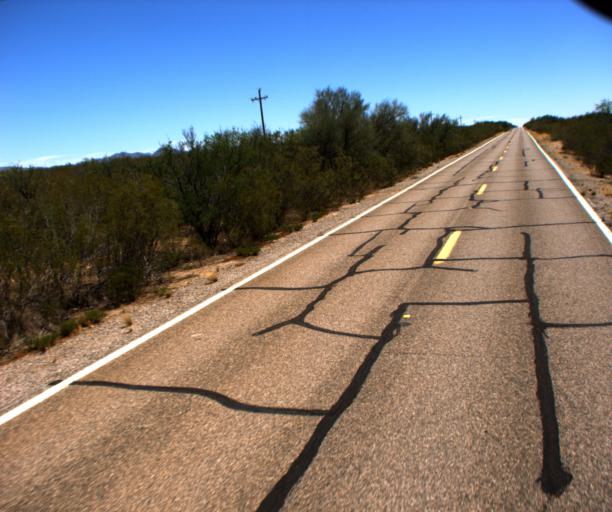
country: US
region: Arizona
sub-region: Pima County
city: Three Points
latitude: 31.9539
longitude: -111.3887
